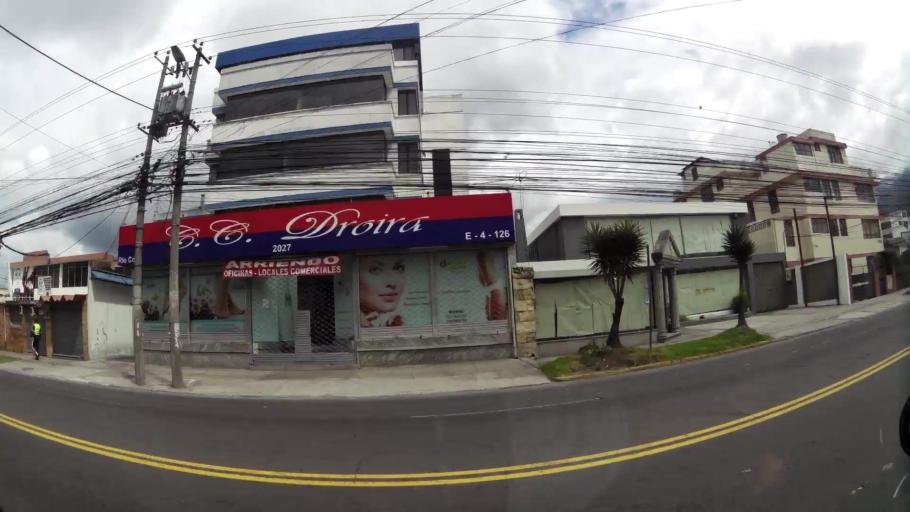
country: EC
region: Pichincha
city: Quito
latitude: -0.1620
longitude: -78.4827
